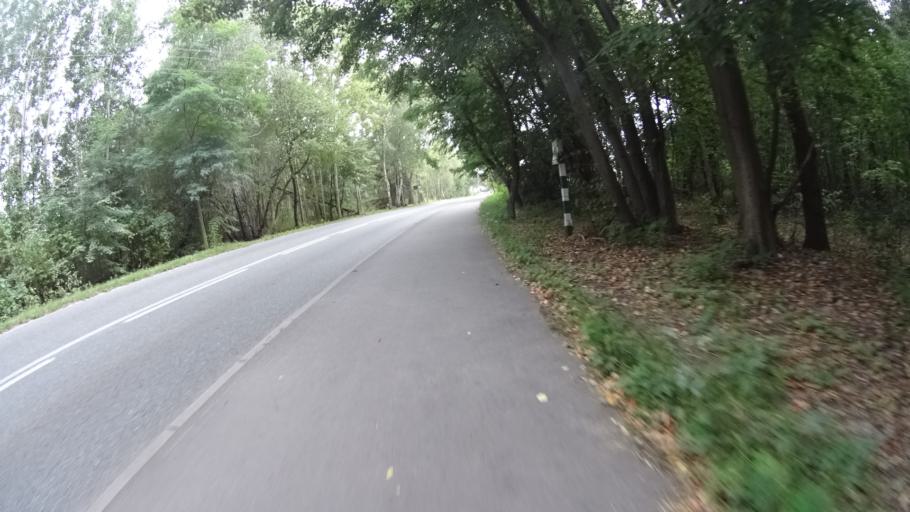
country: PL
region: Masovian Voivodeship
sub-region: Powiat pruszkowski
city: Granica
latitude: 52.1215
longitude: 20.7975
